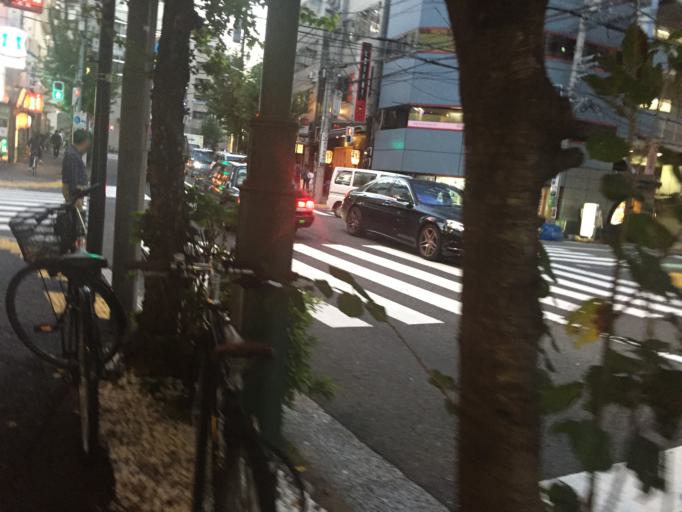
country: JP
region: Tokyo
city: Tokyo
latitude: 35.6457
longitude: 139.7079
